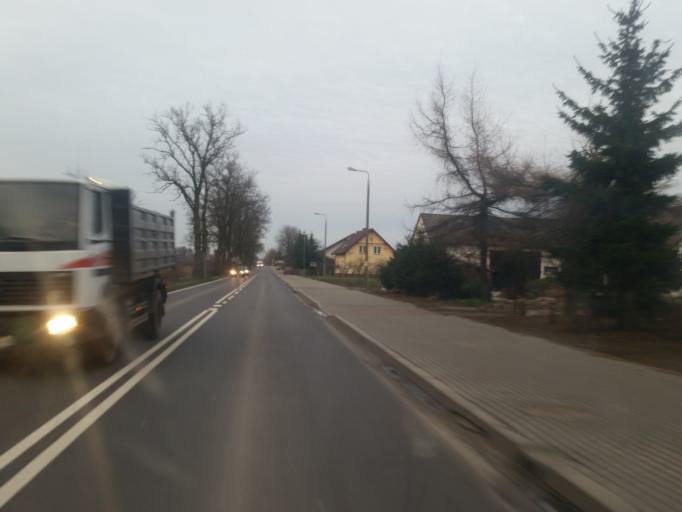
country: PL
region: Kujawsko-Pomorskie
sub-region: Powiat brodnicki
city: Brodnica
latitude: 53.1704
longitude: 19.3865
